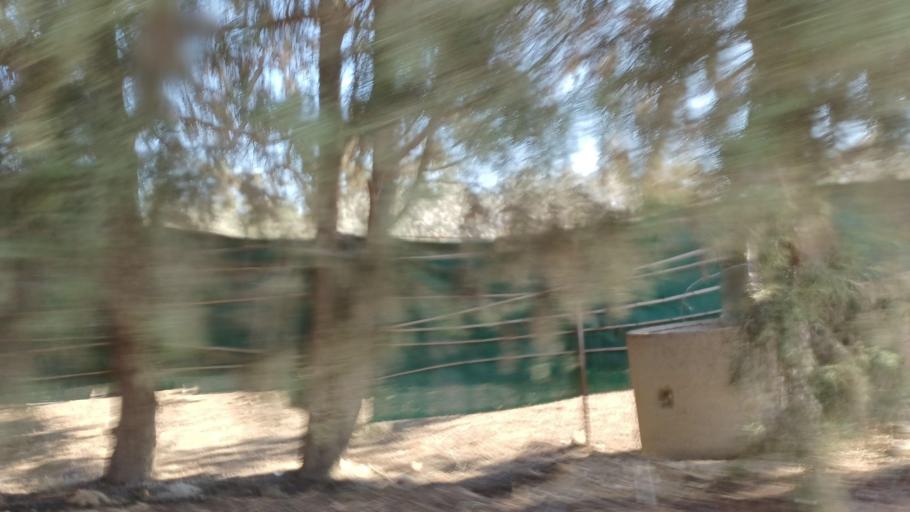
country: CY
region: Larnaka
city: Voroklini
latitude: 34.9972
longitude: 33.6718
